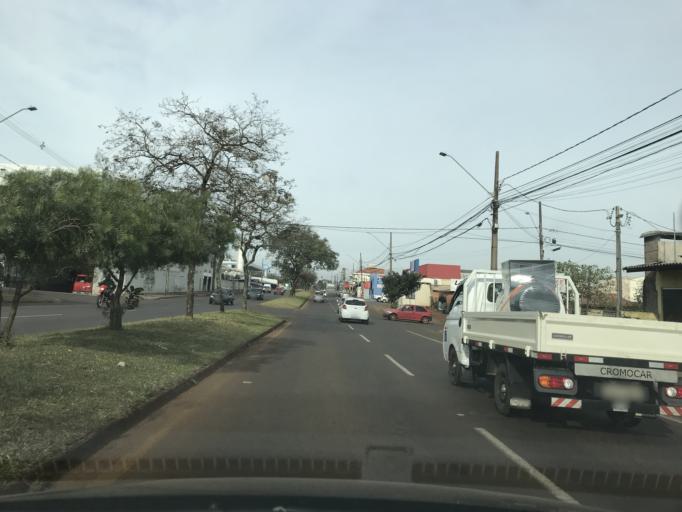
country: BR
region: Parana
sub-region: Cascavel
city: Cascavel
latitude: -24.9658
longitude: -53.4835
